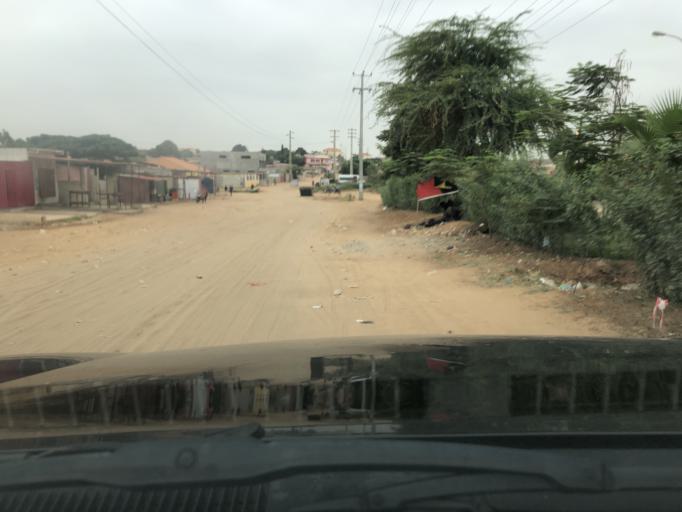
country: AO
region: Luanda
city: Luanda
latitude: -8.9409
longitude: 13.2394
